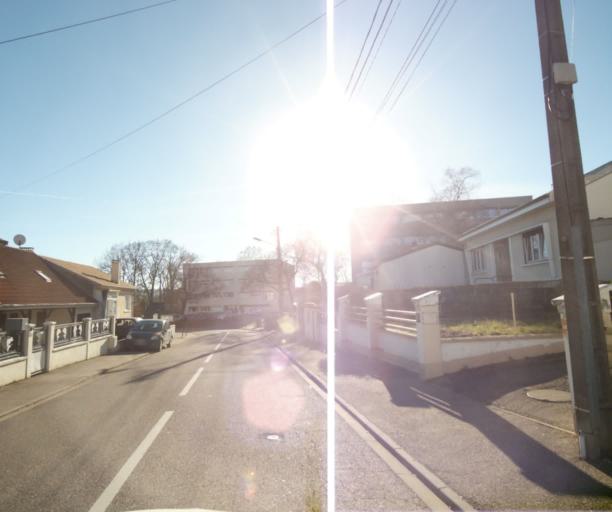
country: FR
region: Lorraine
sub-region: Departement de Meurthe-et-Moselle
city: Laneuveville-devant-Nancy
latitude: 48.6569
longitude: 6.2220
